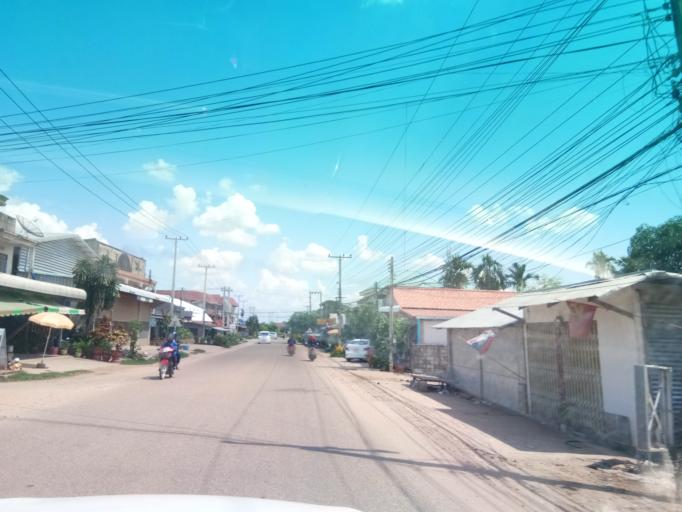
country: LA
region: Savannahkhet
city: Savannakhet
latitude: 16.5806
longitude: 104.7472
